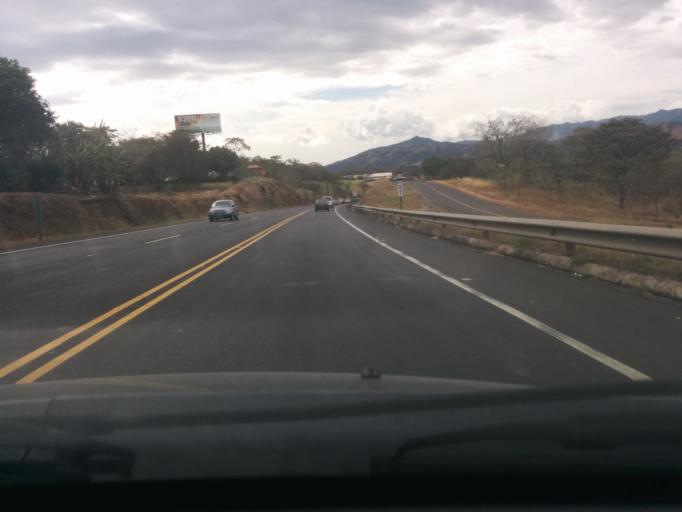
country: CR
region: Alajuela
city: Atenas
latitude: 9.9634
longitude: -84.3203
